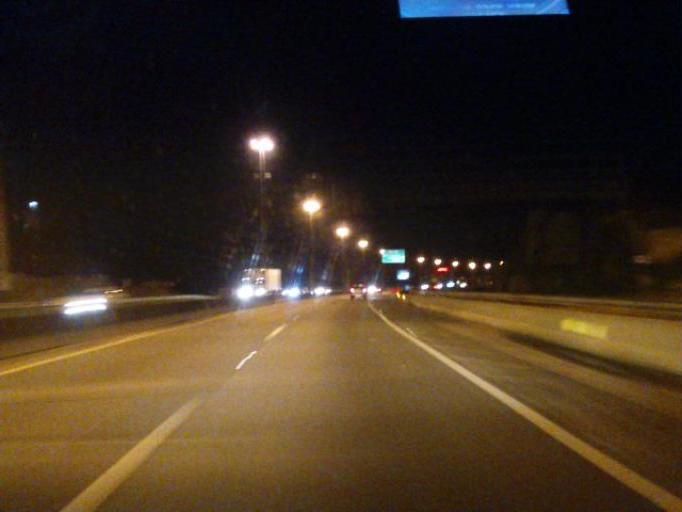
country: BR
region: Santa Catarina
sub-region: Balneario Camboriu
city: Balneario Camboriu
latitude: -27.0077
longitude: -48.6181
